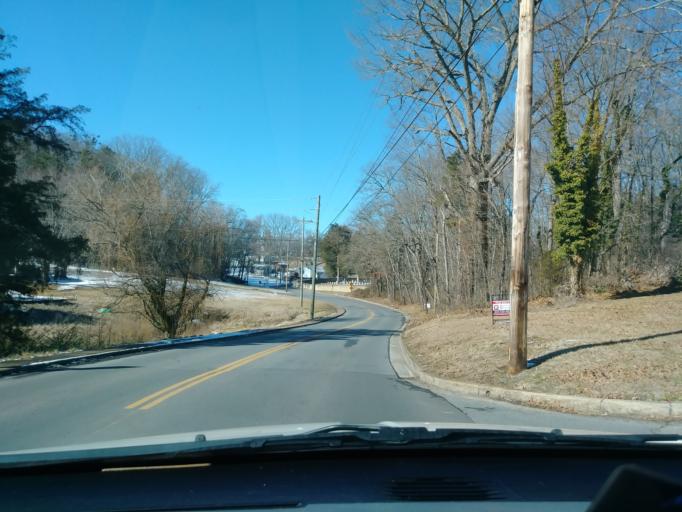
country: US
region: Tennessee
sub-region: Greene County
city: Greeneville
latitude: 36.1530
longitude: -82.8385
